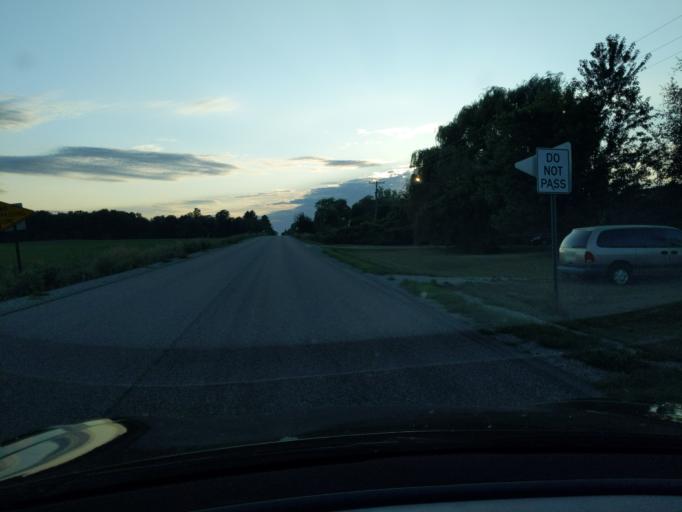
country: US
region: Michigan
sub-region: Gratiot County
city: Saint Louis
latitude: 43.3788
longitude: -84.5793
